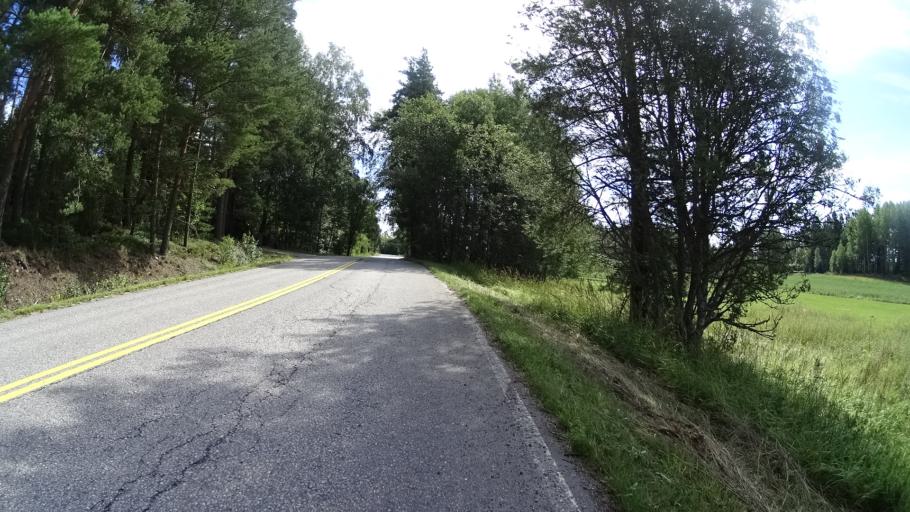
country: FI
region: Uusimaa
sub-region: Helsinki
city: Kirkkonummi
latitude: 60.0987
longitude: 24.4960
